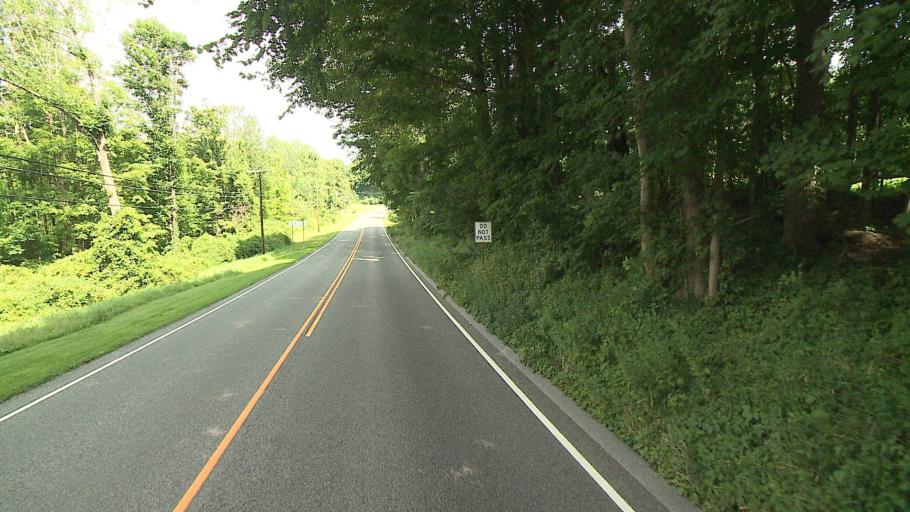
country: US
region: Connecticut
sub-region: Fairfield County
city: Sherman
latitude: 41.5841
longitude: -73.4984
